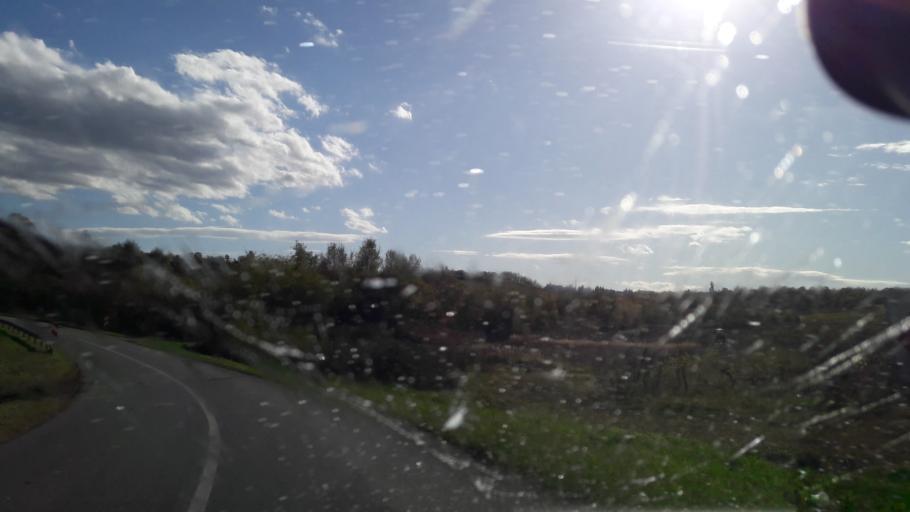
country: HR
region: Osjecko-Baranjska
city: Gorjani
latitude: 45.3856
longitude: 18.2485
